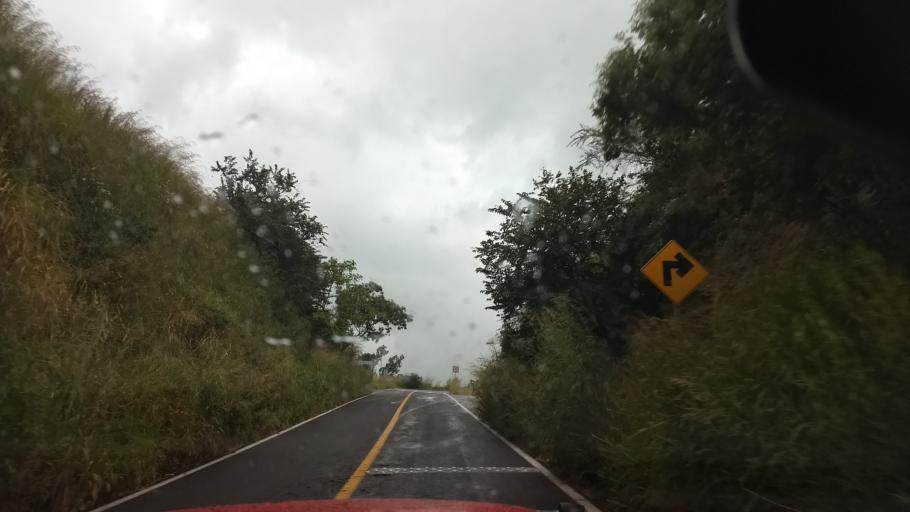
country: MX
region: Jalisco
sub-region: Tonila
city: San Marcos
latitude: 19.4352
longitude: -103.4952
